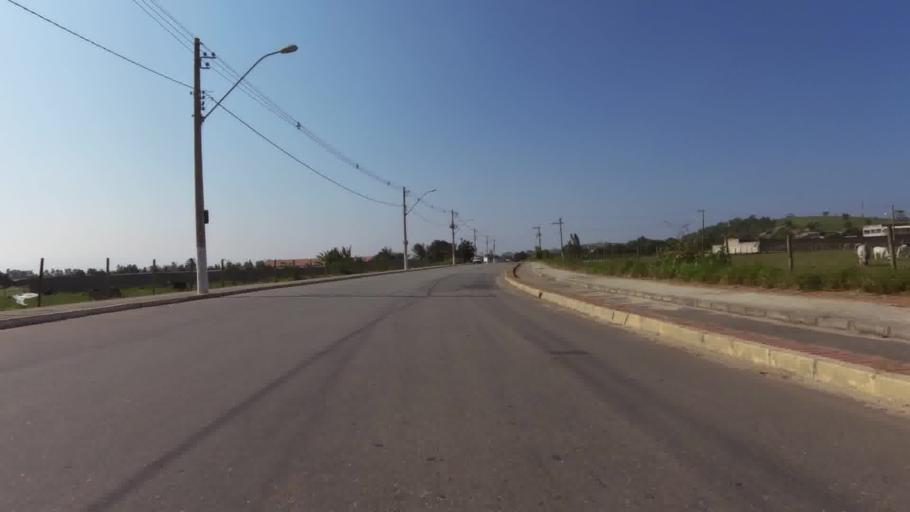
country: BR
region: Espirito Santo
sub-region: Itapemirim
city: Itapemirim
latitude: -21.0170
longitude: -40.8397
